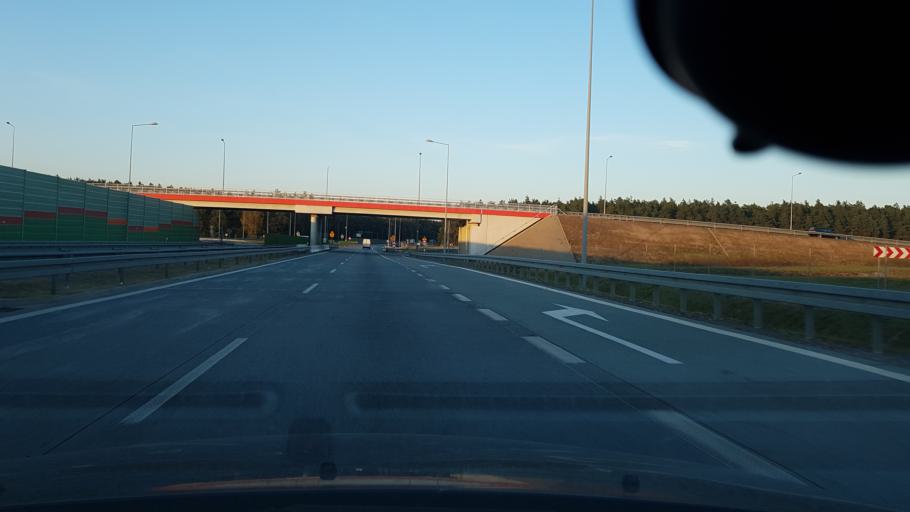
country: PL
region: Lodz Voivodeship
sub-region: Powiat tomaszowski
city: Lubochnia
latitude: 51.6231
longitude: 20.0951
